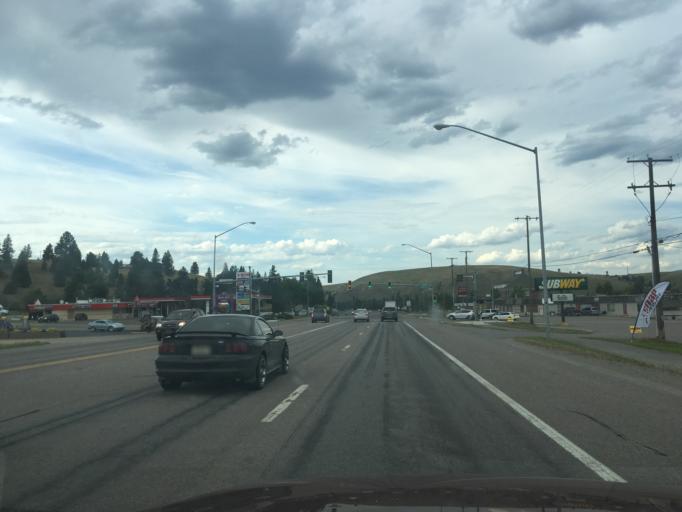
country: US
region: Montana
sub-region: Missoula County
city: Lolo
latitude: 46.7642
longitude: -114.0806
